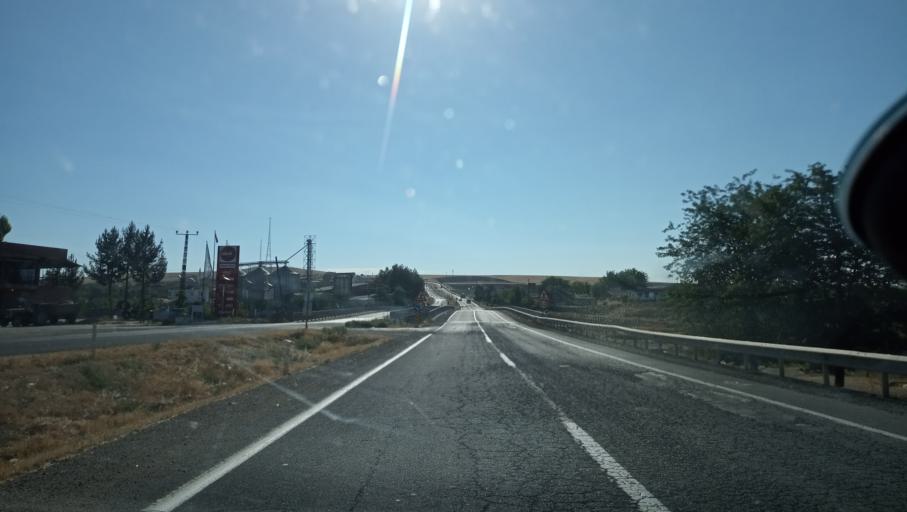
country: TR
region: Diyarbakir
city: Sur
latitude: 37.9909
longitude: 40.3816
